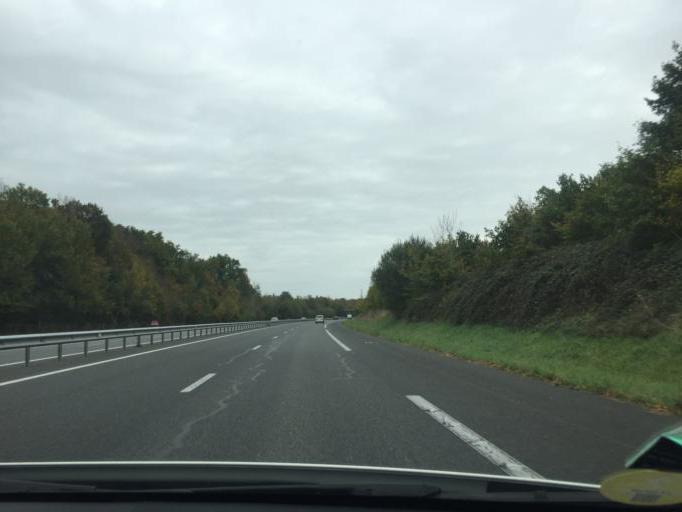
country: FR
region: Bourgogne
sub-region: Departement de l'Yonne
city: Egriselles-le-Bocage
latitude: 48.1133
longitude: 3.1344
